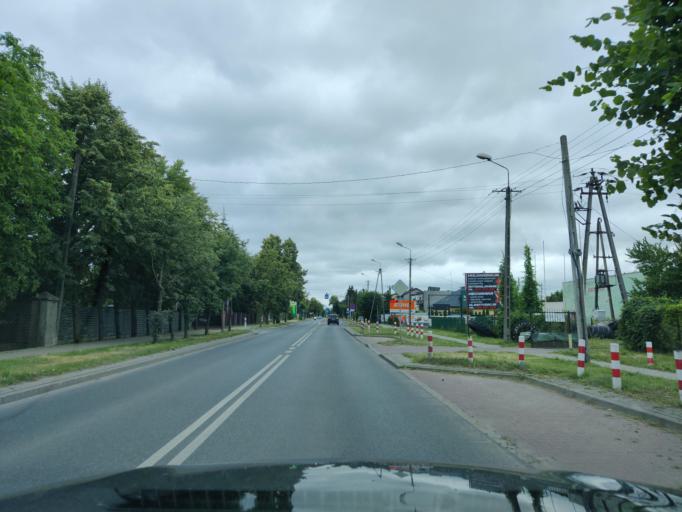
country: PL
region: Masovian Voivodeship
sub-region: Powiat pultuski
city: Pultusk
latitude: 52.6944
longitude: 21.0811
